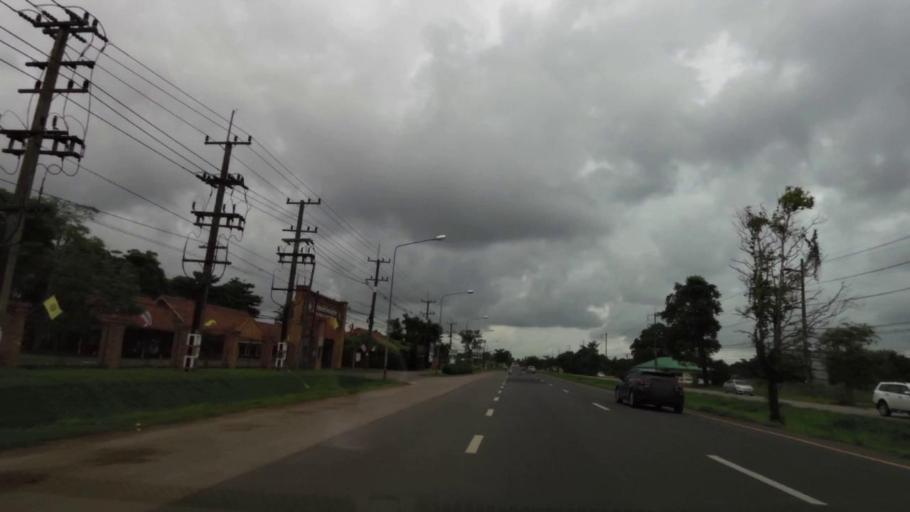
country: TH
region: Chanthaburi
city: Tha Mai
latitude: 12.6629
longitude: 102.0087
